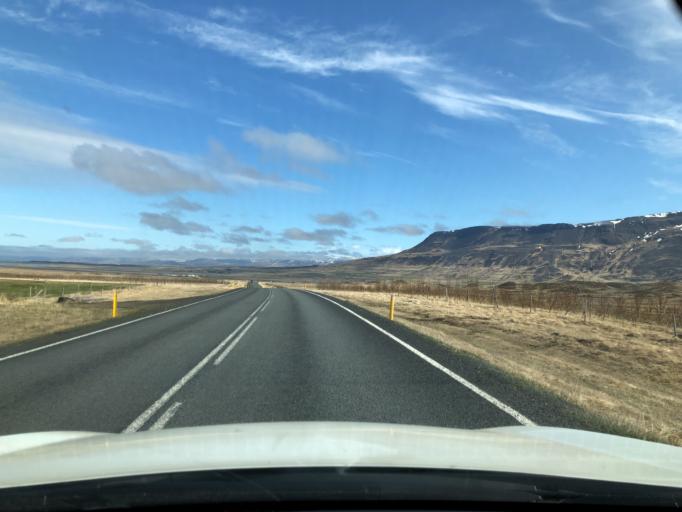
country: IS
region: Northwest
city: Saudarkrokur
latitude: 65.4950
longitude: -20.4089
